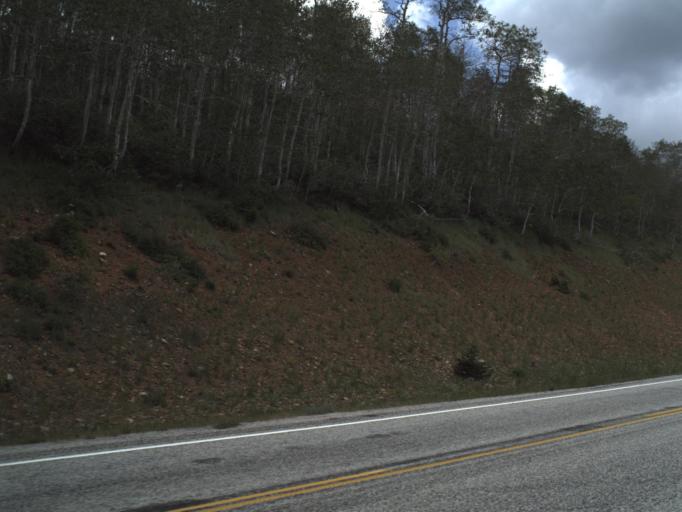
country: US
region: Utah
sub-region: Weber County
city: Wolf Creek
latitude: 41.4099
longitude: -111.5283
